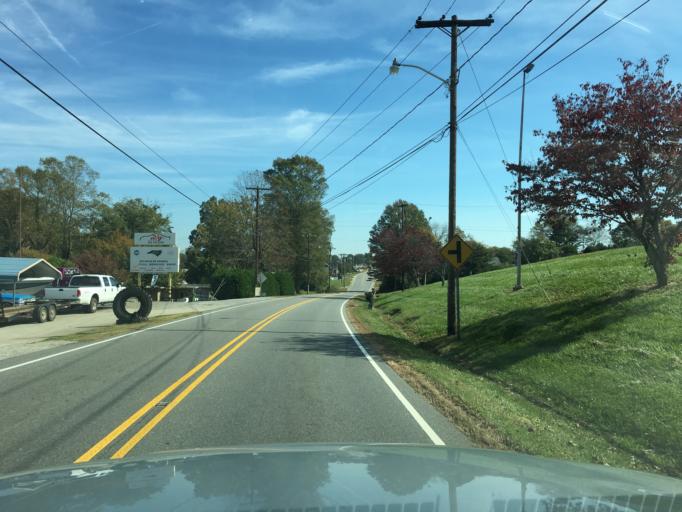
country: US
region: North Carolina
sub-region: Catawba County
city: Saint Stephens
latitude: 35.7334
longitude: -81.2977
